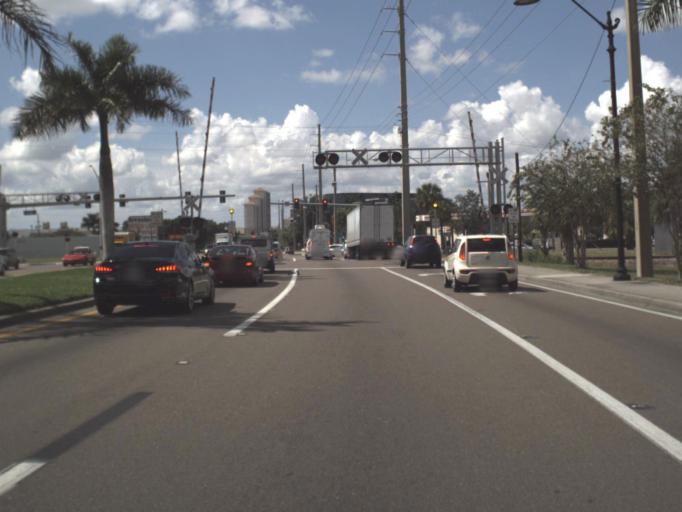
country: US
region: Florida
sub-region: Lee County
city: Fort Myers
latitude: 26.6411
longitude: -81.8593
